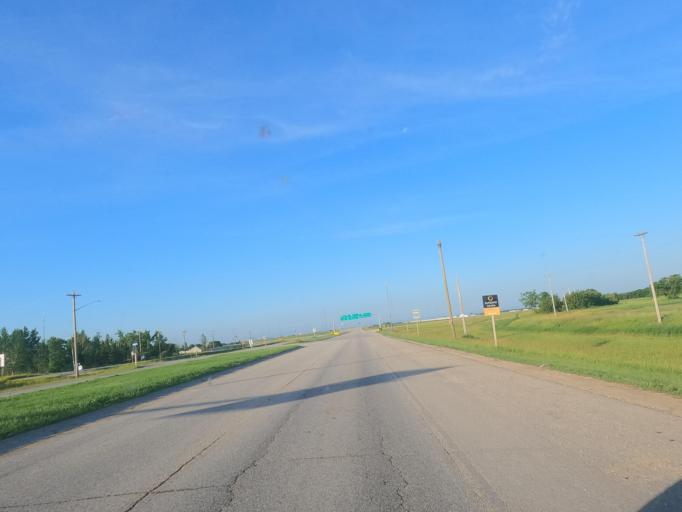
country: CA
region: Manitoba
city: Winnipeg
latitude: 49.9937
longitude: -97.1017
